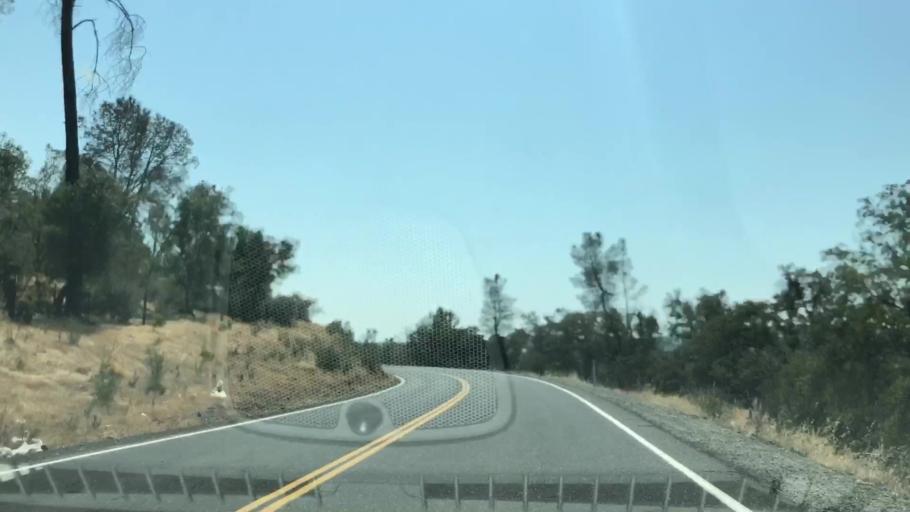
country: US
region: California
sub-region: Calaveras County
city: Copperopolis
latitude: 37.9540
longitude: -120.6140
